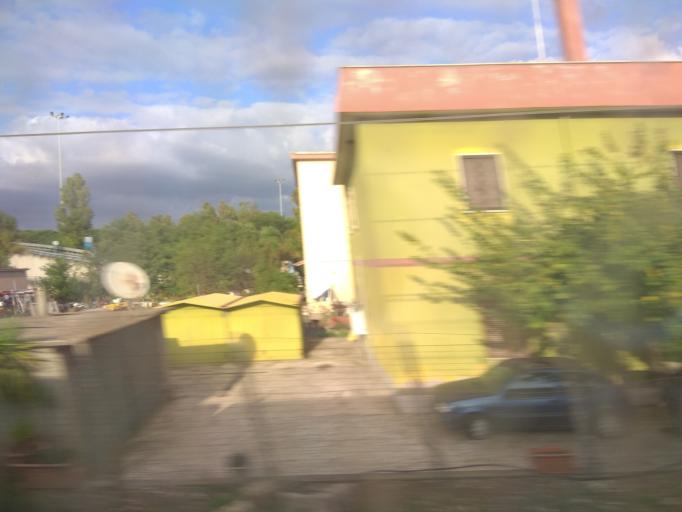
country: IT
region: Latium
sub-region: Citta metropolitana di Roma Capitale
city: Maccarese
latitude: 41.9131
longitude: 12.2025
